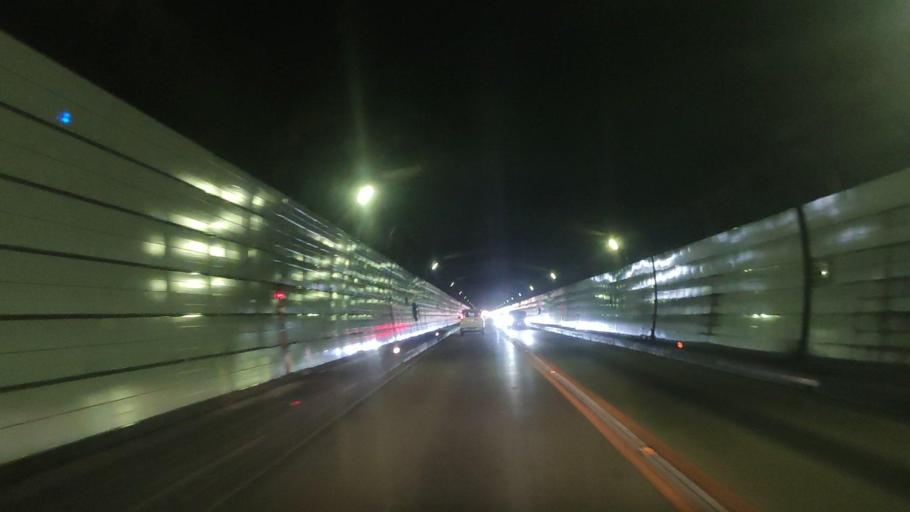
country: JP
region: Kumamoto
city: Hitoyoshi
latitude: 32.0960
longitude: 130.8031
